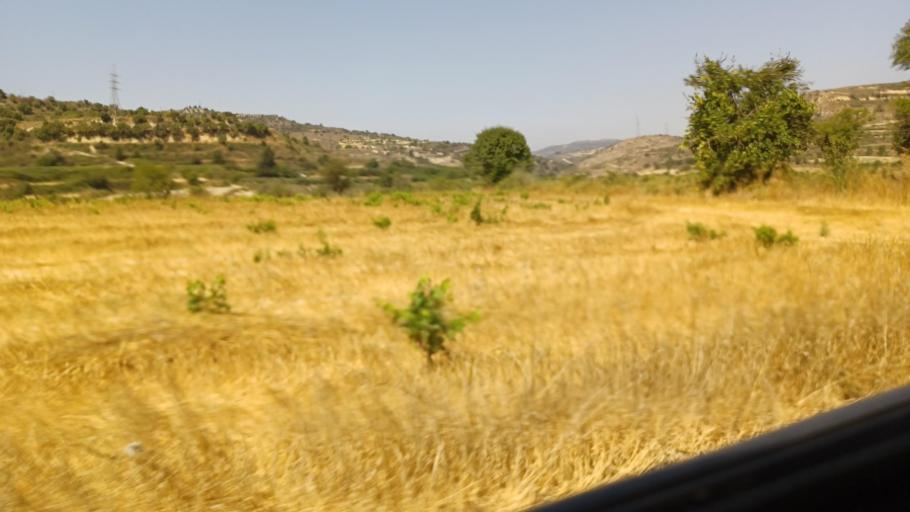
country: CY
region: Pafos
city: Mesogi
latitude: 34.8678
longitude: 32.4946
